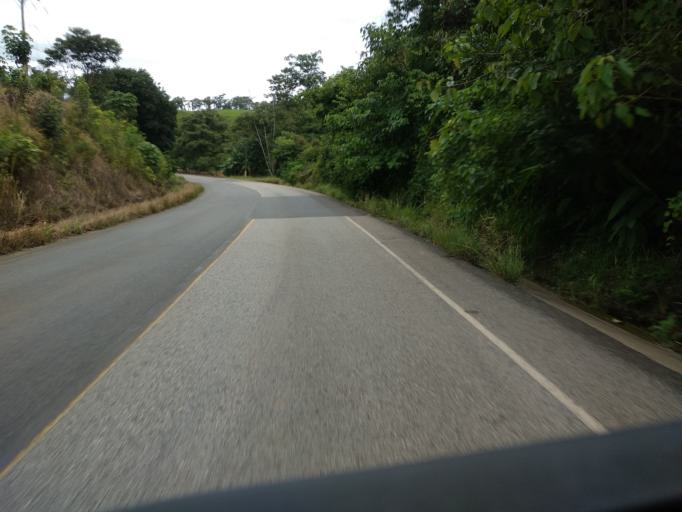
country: CR
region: Puntarenas
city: Buenos Aires
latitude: 9.0970
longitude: -83.2797
